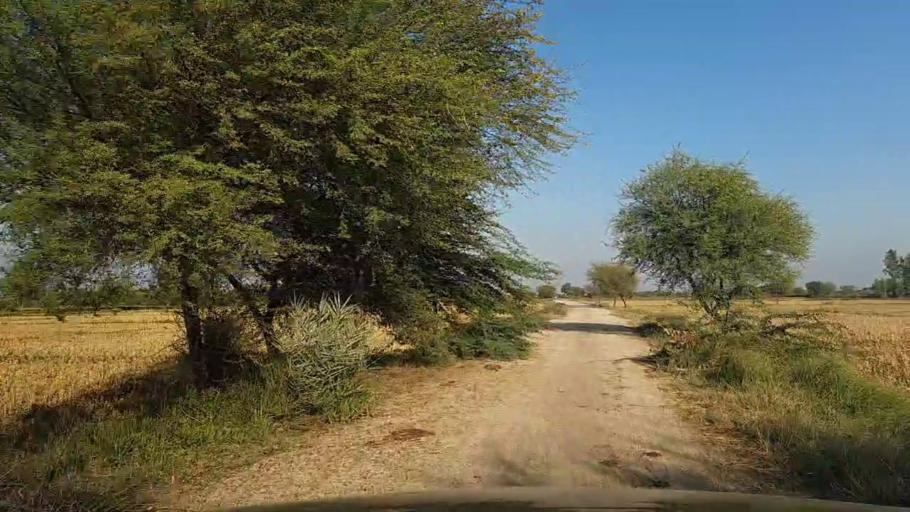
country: PK
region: Sindh
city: Mirpur Batoro
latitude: 24.6835
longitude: 68.3609
